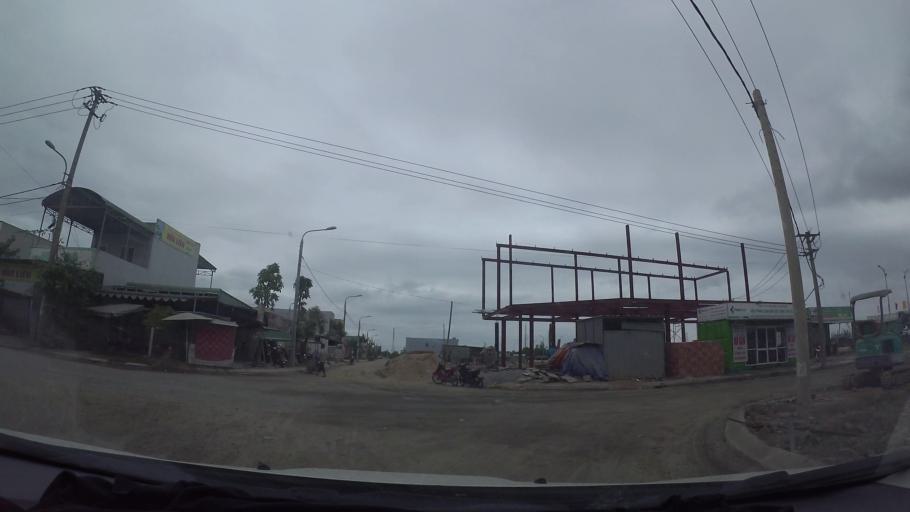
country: VN
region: Da Nang
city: Lien Chieu
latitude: 16.0912
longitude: 108.1073
